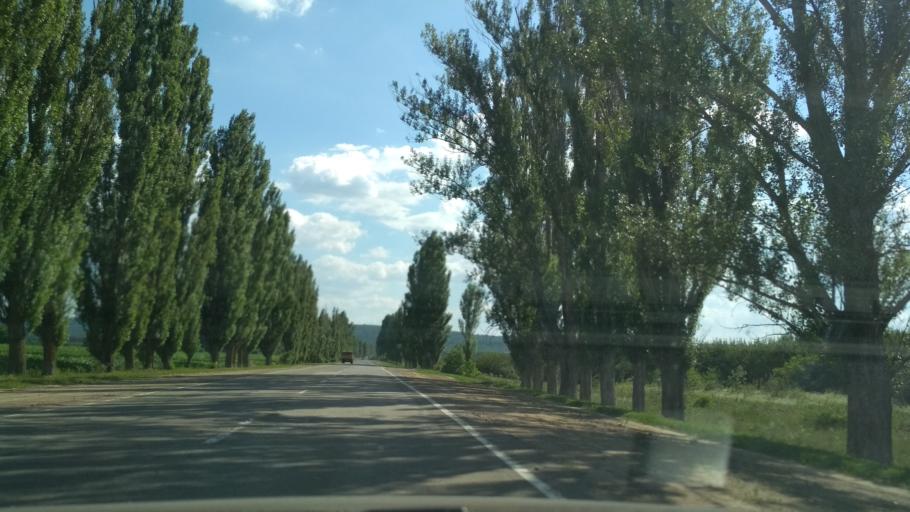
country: MD
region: Chisinau
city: Vadul lui Voda
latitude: 47.1072
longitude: 29.1014
